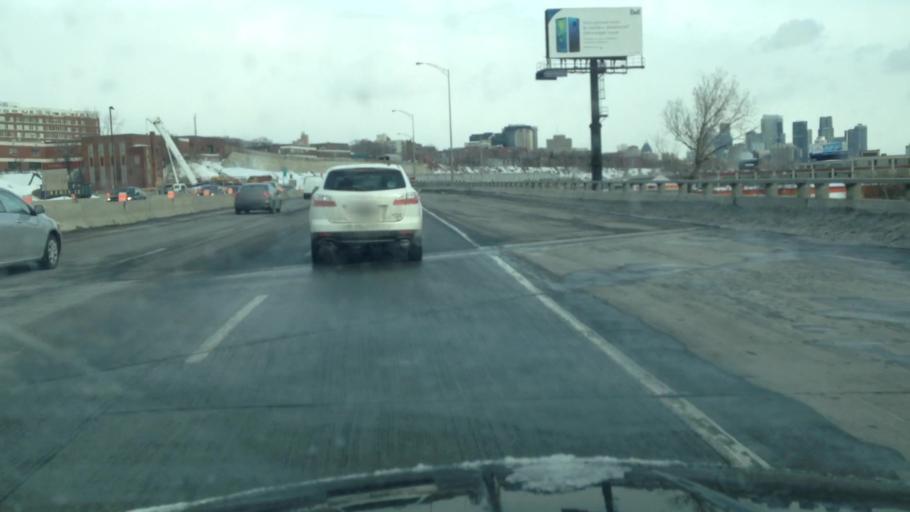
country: CA
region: Quebec
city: Westmount
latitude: 45.4743
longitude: -73.5958
